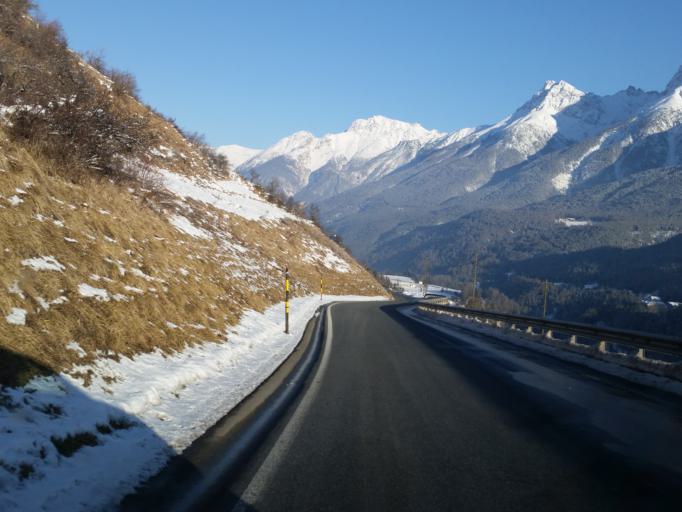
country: CH
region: Grisons
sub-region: Inn District
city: Scuol
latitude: 46.7907
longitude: 10.2640
